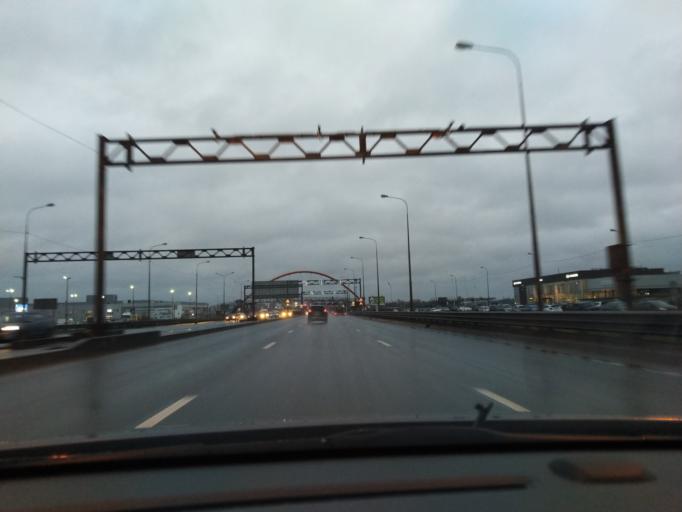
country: RU
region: St.-Petersburg
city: Sosnovaya Polyana
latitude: 59.8058
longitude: 30.1639
